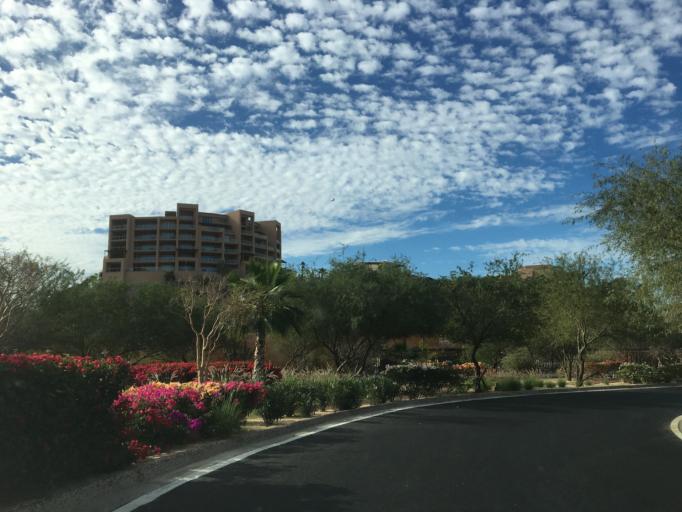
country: MX
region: Baja California Sur
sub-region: La Paz
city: La Paz
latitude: 24.2145
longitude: -110.2966
